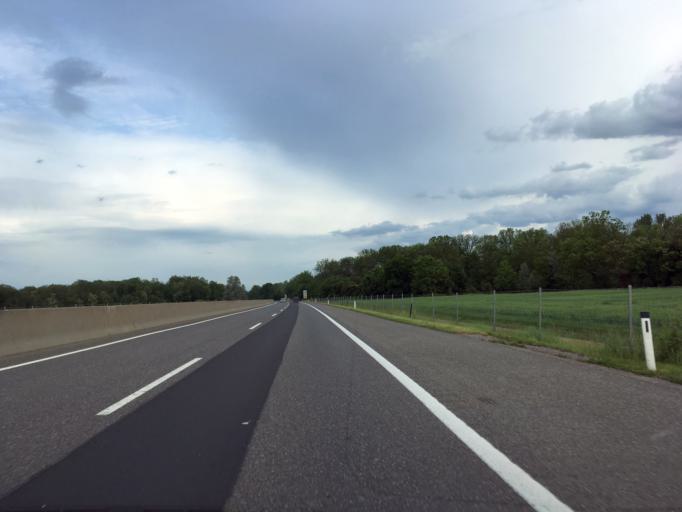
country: AT
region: Lower Austria
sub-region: Politischer Bezirk Tulln
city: Kirchberg am Wagram
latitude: 48.3773
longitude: 15.9287
